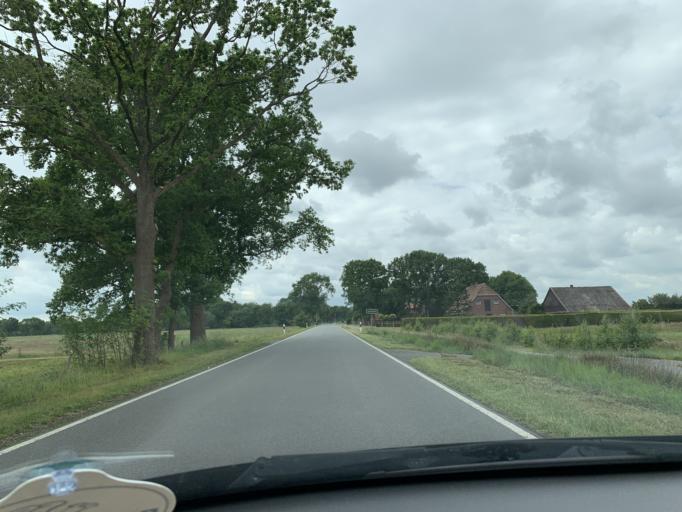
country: DE
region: Lower Saxony
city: Bockhorn
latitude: 53.3181
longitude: 8.0153
